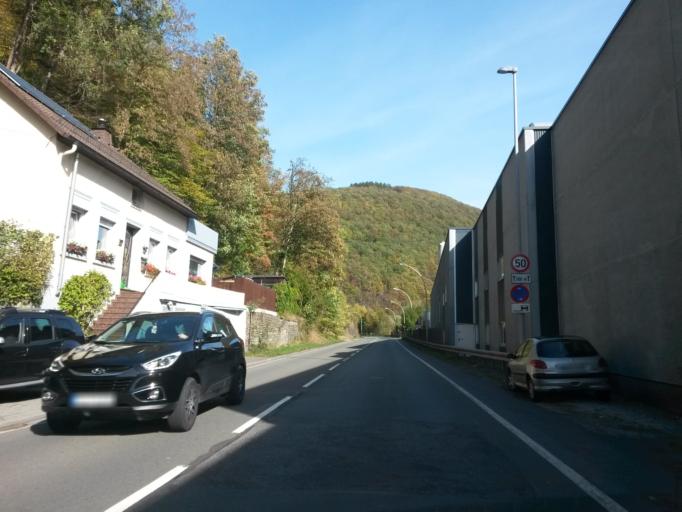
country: DE
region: North Rhine-Westphalia
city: Plettenberg
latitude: 51.2342
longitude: 7.8778
